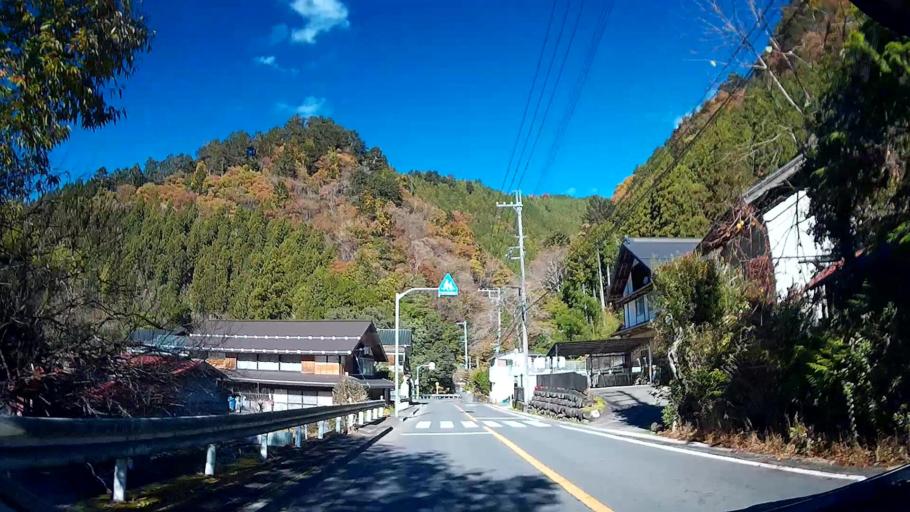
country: JP
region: Yamanashi
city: Uenohara
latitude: 35.7030
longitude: 139.1320
